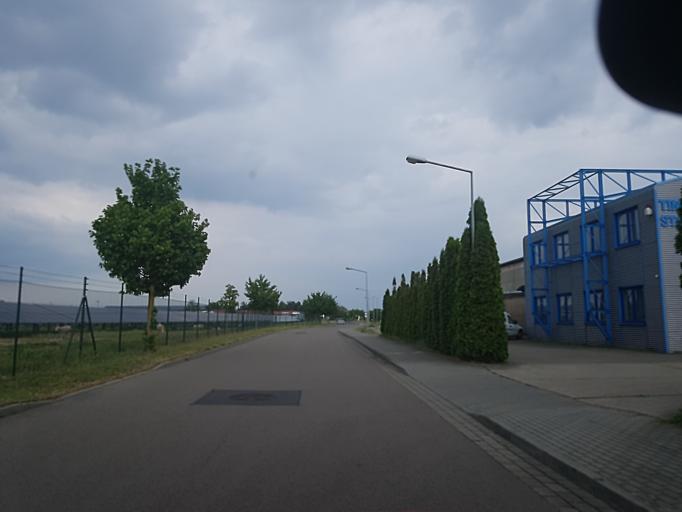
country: DE
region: Saxony-Anhalt
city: Elster
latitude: 51.8329
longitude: 12.8116
